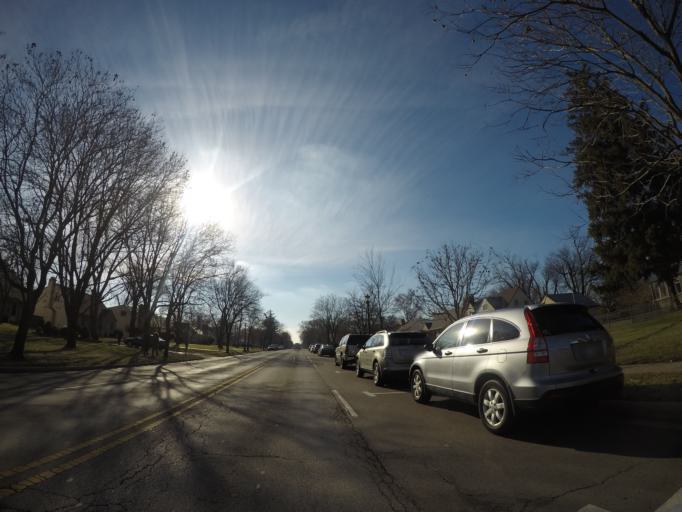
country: US
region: Ohio
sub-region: Franklin County
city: Upper Arlington
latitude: 40.0143
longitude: -83.0578
